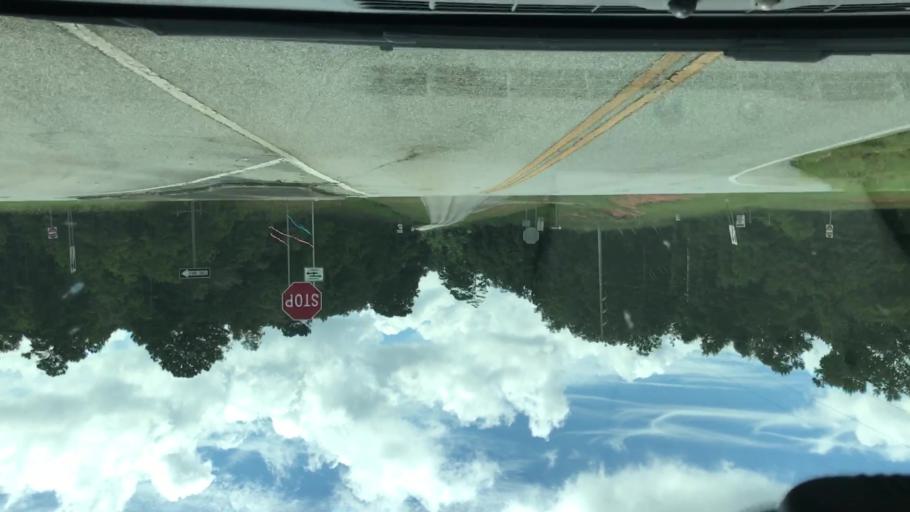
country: US
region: Georgia
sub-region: Stewart County
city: Lumpkin
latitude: 32.0551
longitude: -84.8065
